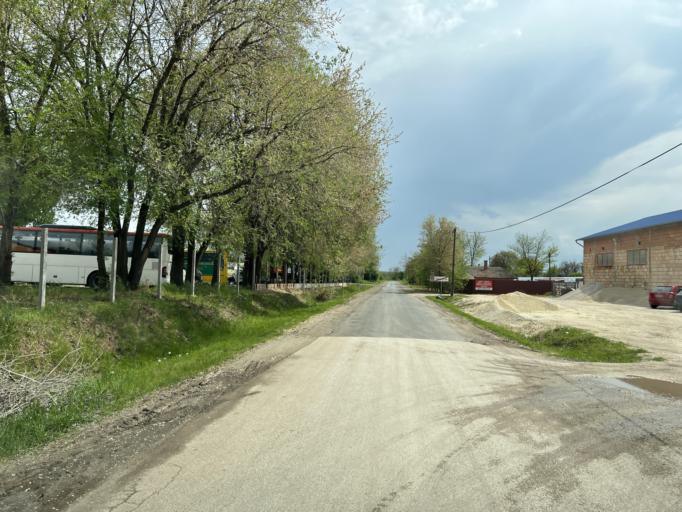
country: HU
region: Pest
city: Nagykoros
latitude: 47.0195
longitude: 19.7915
